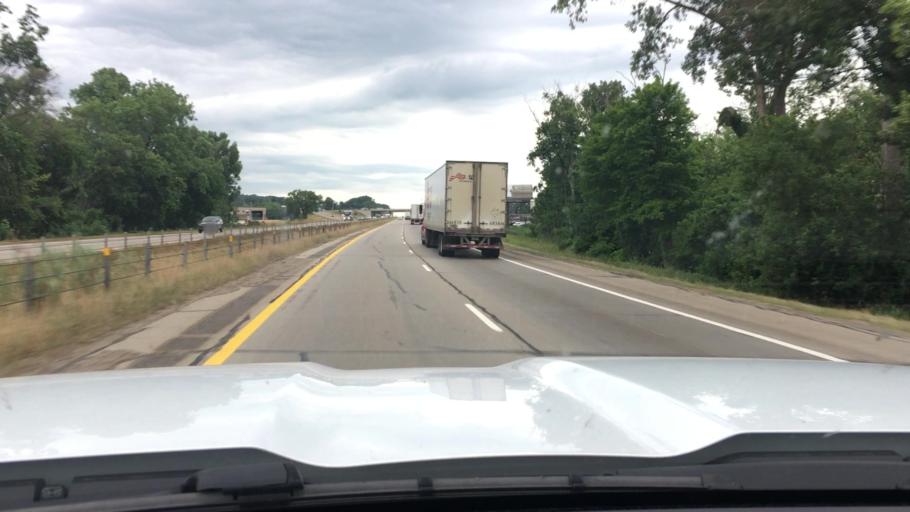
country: US
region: Michigan
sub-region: Kent County
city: Cutlerville
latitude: 42.8184
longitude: -85.6690
